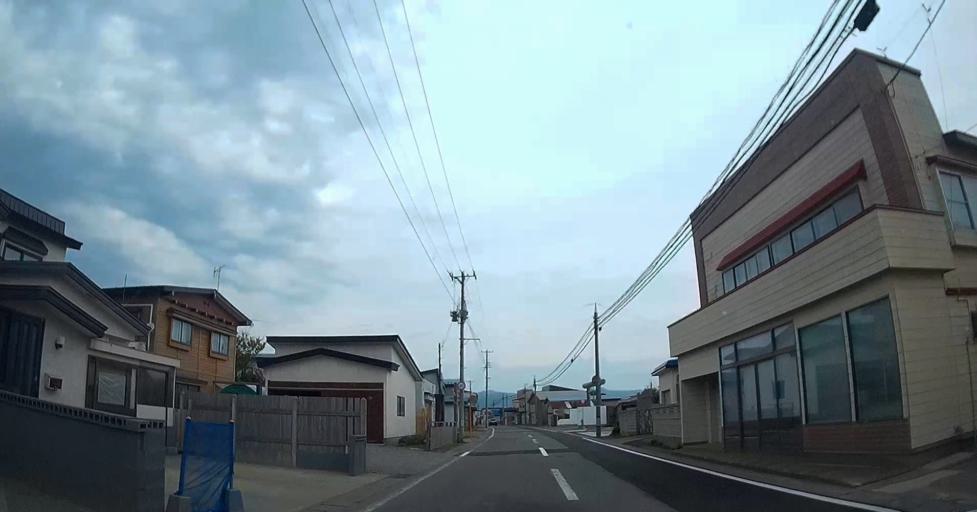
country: JP
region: Aomori
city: Shimokizukuri
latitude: 41.0322
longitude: 140.3279
